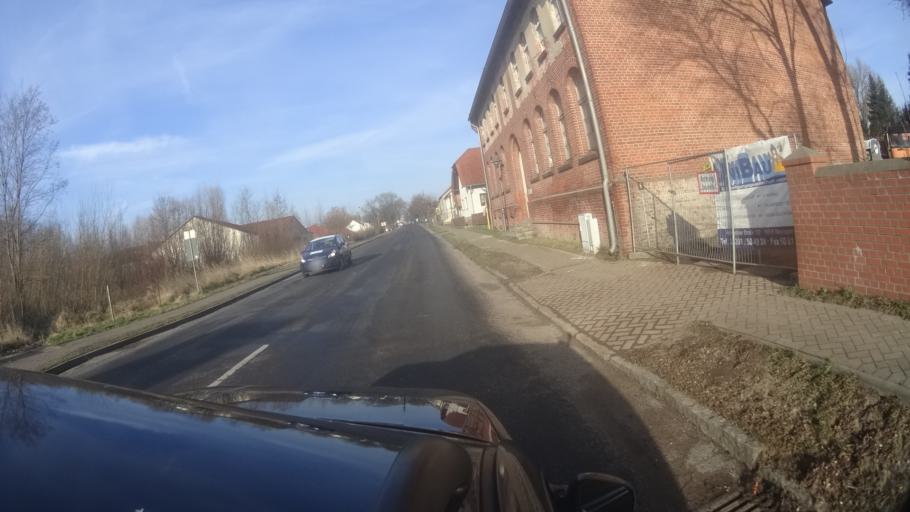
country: DE
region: Brandenburg
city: Velten
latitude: 52.7181
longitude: 13.1004
